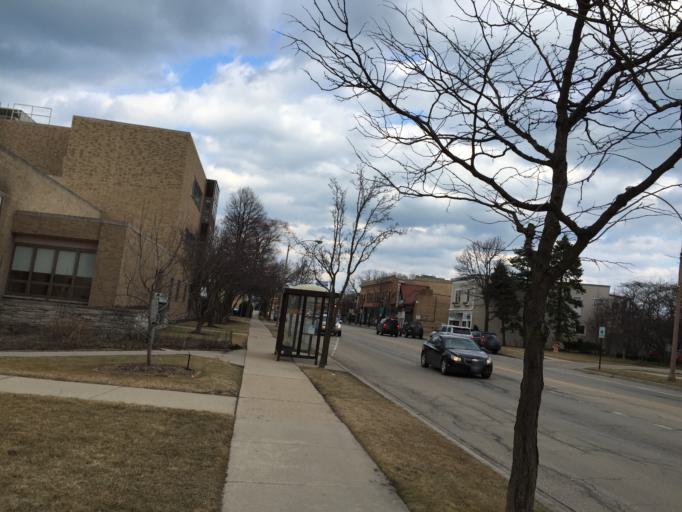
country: US
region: Illinois
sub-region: Cook County
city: Wilmette
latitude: 42.0745
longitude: -87.7095
